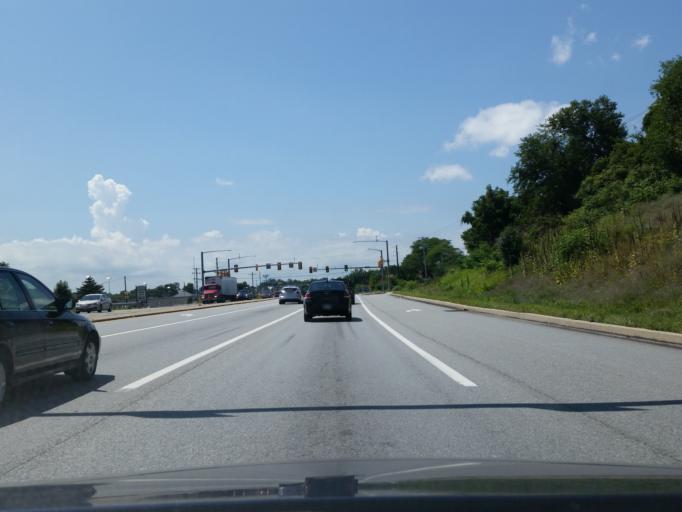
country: US
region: Pennsylvania
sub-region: York County
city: North York
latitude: 39.9828
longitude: -76.7137
